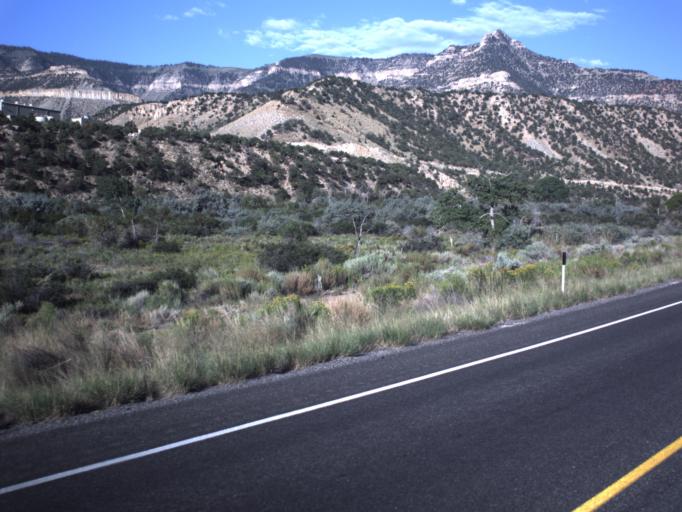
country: US
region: Utah
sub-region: Emery County
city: Huntington
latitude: 39.3680
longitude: -111.0522
